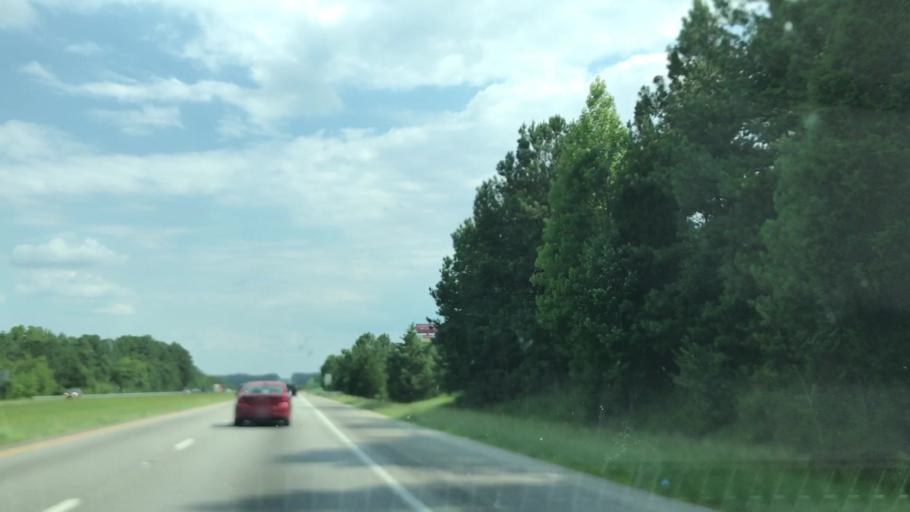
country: US
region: South Carolina
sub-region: Chester County
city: Great Falls
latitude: 34.6004
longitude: -81.0177
